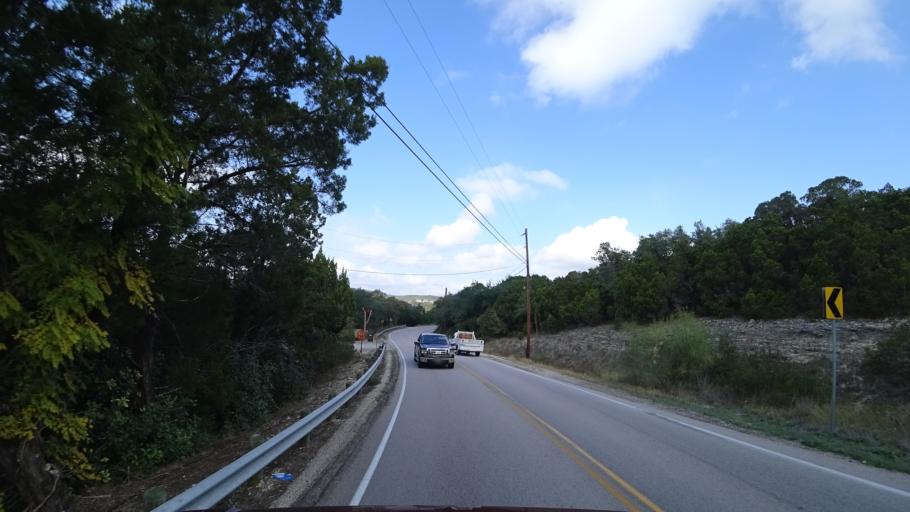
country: US
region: Texas
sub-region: Travis County
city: Hudson Bend
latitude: 30.4289
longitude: -97.8731
